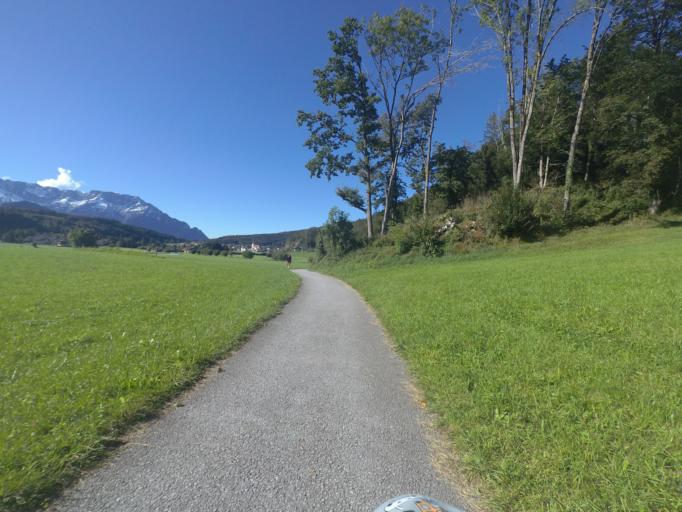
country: AT
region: Salzburg
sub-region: Politischer Bezirk Hallein
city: Adnet
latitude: 47.6896
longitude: 13.1446
